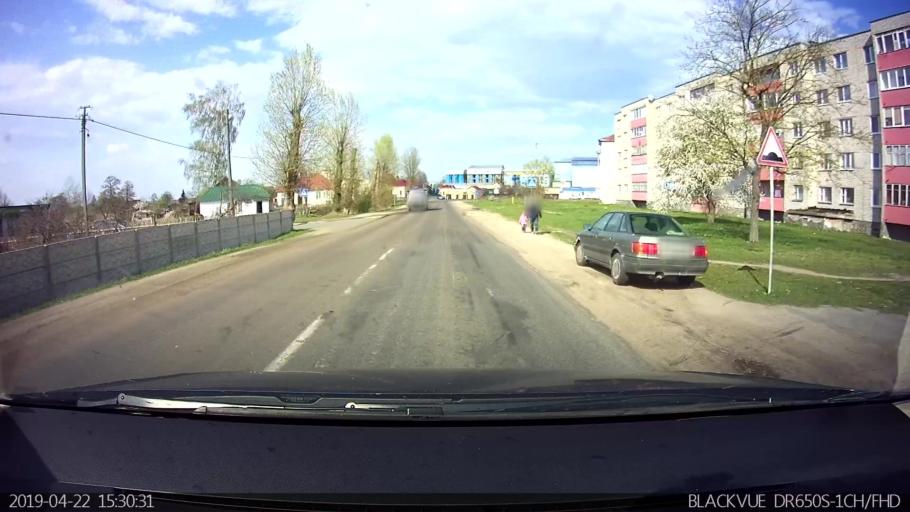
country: BY
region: Brest
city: Vysokaye
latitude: 52.3986
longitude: 23.3797
